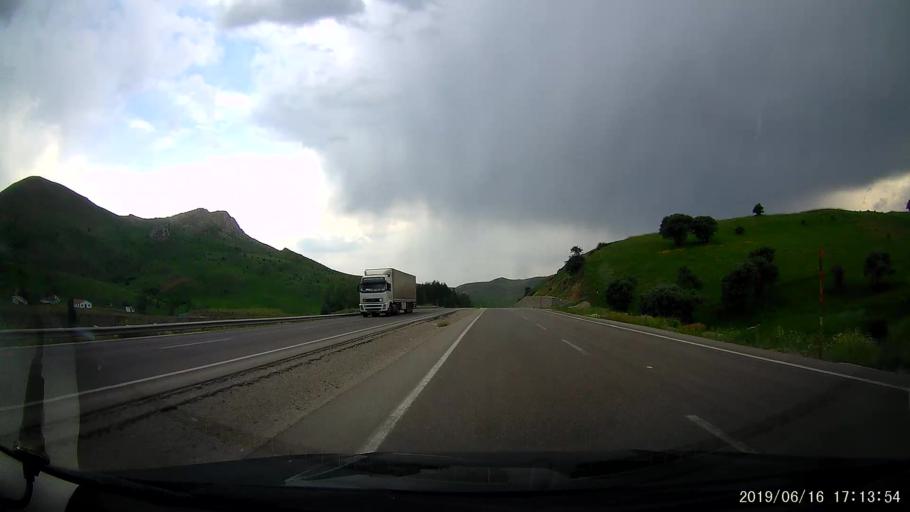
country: TR
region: Erzurum
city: Askale
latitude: 39.8553
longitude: 40.5880
